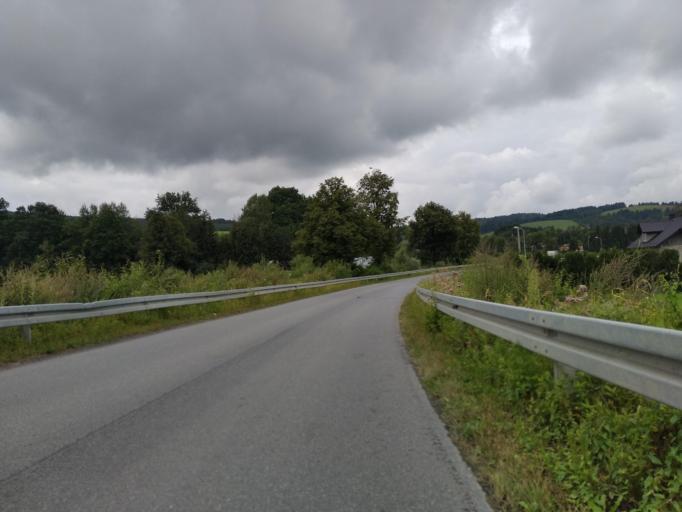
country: PL
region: Subcarpathian Voivodeship
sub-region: Powiat przemyski
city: Bircza
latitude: 49.6796
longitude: 22.4127
